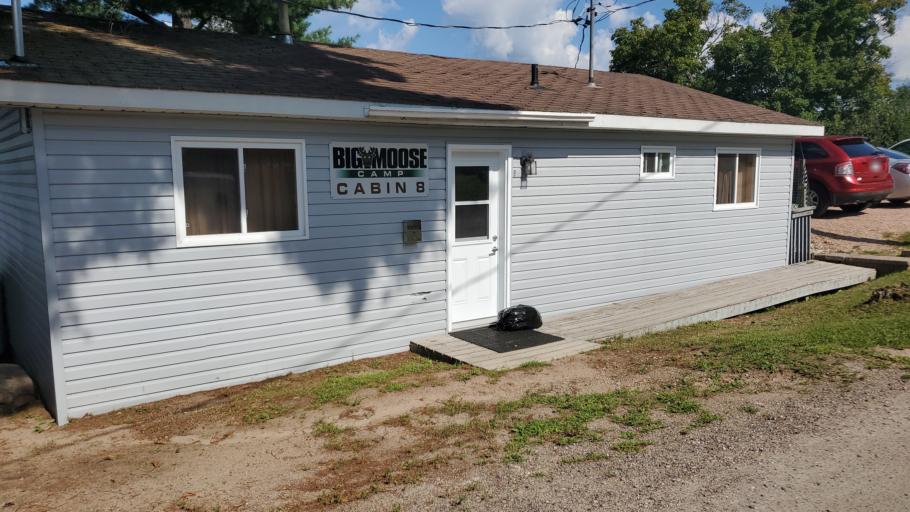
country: CA
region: Ontario
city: Powassan
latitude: 46.2187
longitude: -79.2286
